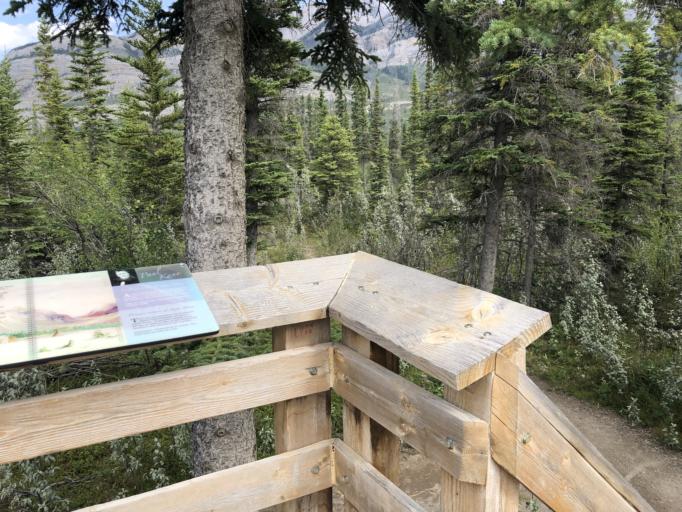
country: CA
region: Alberta
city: Jasper Park Lodge
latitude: 53.1458
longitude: -117.9811
